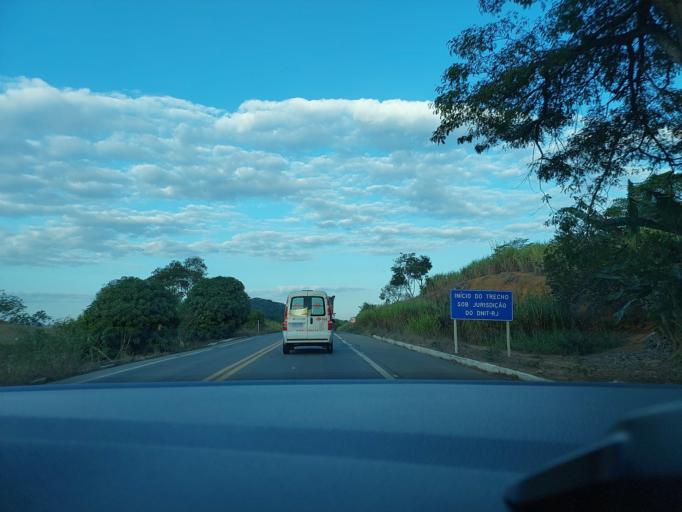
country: BR
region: Minas Gerais
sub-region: Muriae
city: Muriae
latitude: -21.1374
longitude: -42.1789
